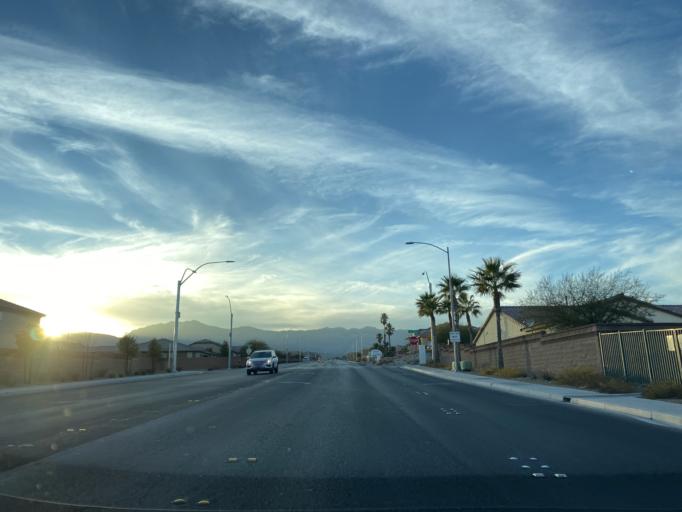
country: US
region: Nevada
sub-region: Clark County
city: Summerlin South
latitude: 36.2847
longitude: -115.3051
